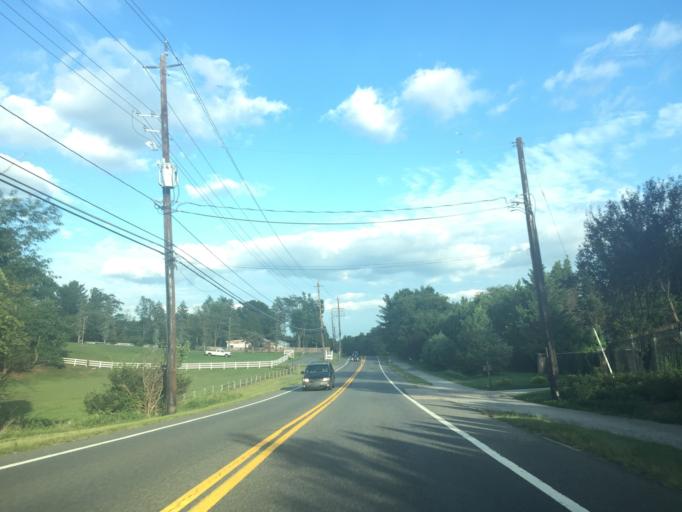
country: US
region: Maryland
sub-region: Montgomery County
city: Redland
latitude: 39.1202
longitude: -77.1106
